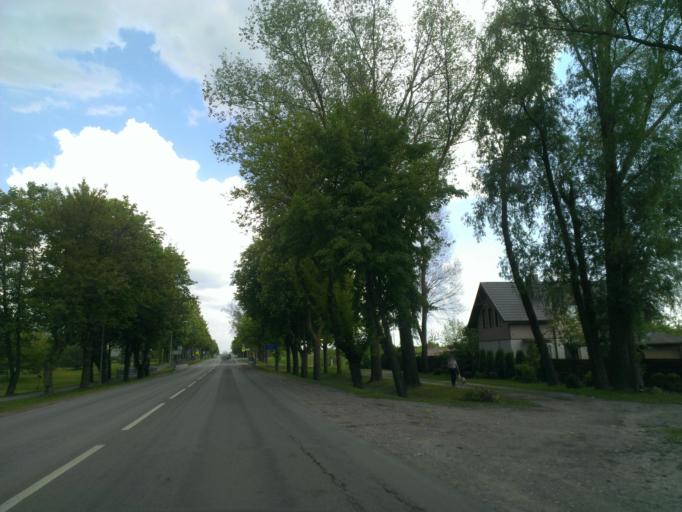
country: LT
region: Klaipedos apskritis
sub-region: Klaipeda
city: Palanga
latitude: 55.9134
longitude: 21.0849
